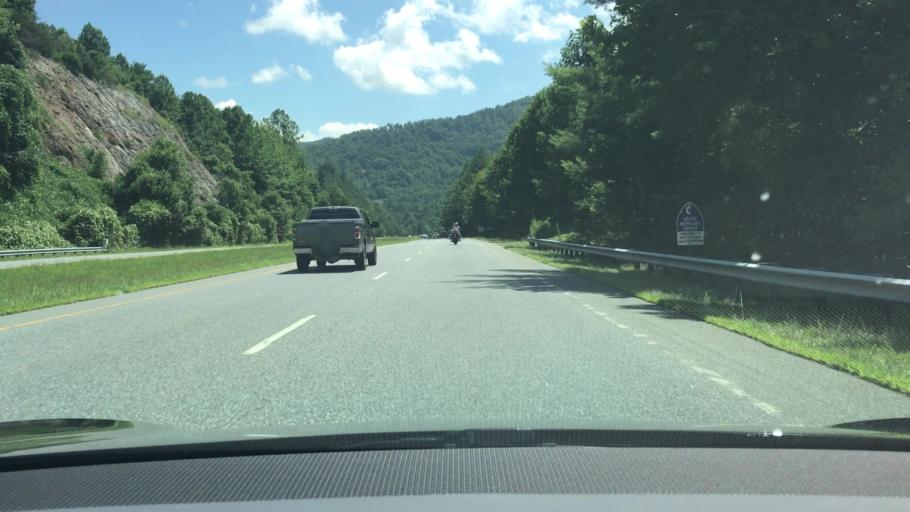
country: US
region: North Carolina
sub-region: Jackson County
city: Sylva
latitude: 35.2923
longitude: -83.2770
